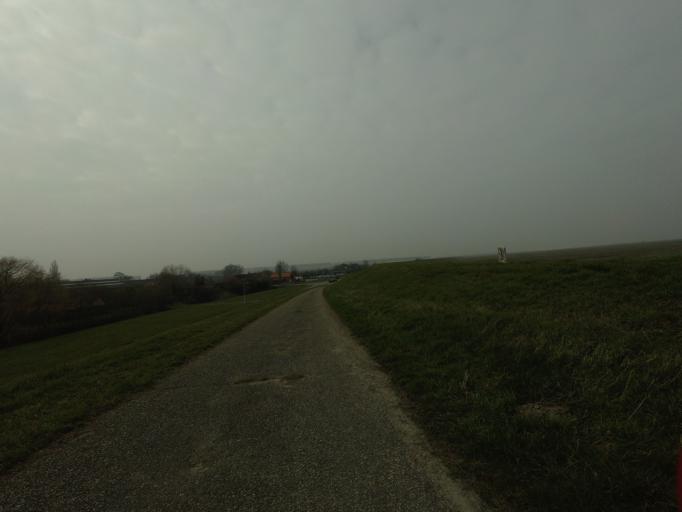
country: NL
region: Zeeland
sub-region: Gemeente Hulst
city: Hulst
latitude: 51.3279
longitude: 4.1514
